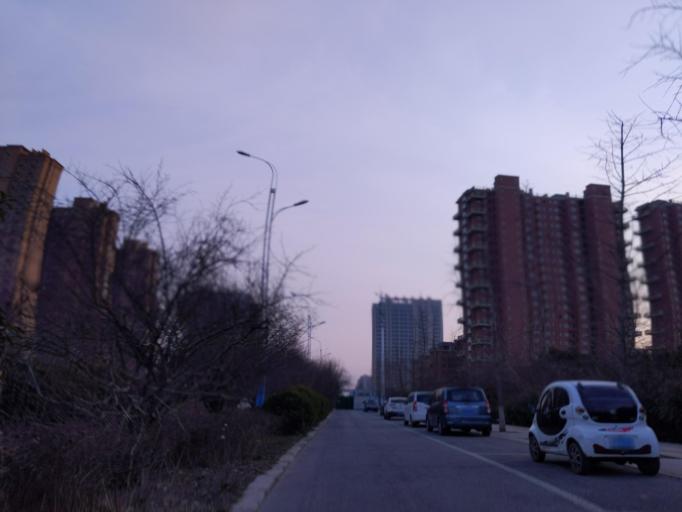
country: CN
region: Henan Sheng
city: Zhongyuanlu
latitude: 35.7837
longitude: 115.1272
